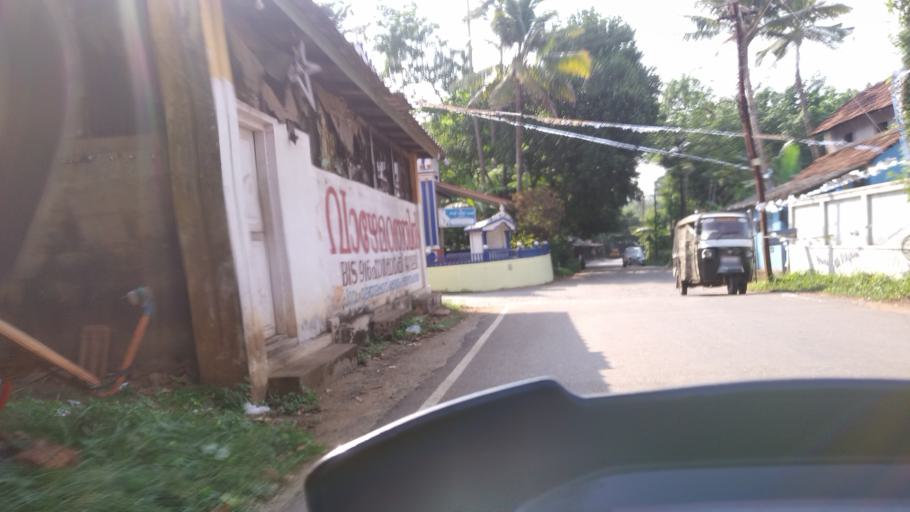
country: IN
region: Kerala
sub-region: Ernakulam
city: Piravam
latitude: 9.8538
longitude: 76.5288
